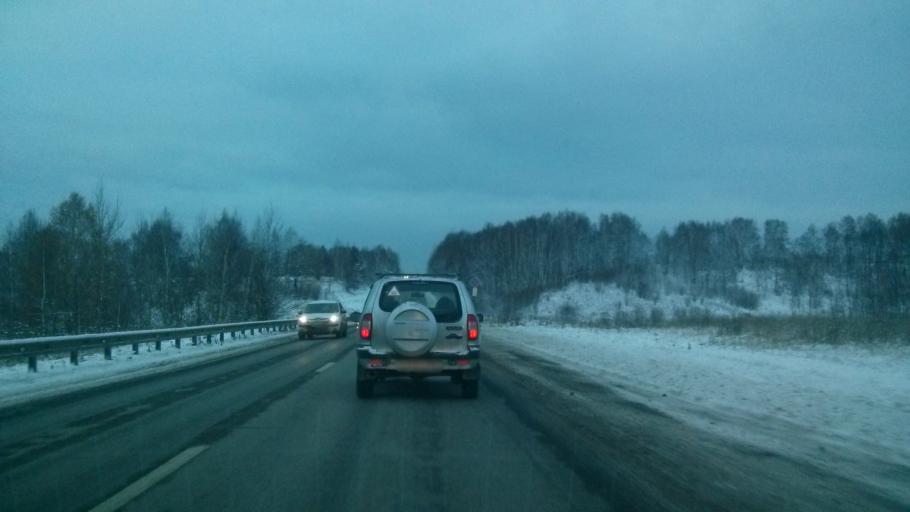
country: RU
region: Nizjnij Novgorod
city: Bogorodsk
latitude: 56.1012
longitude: 43.5850
